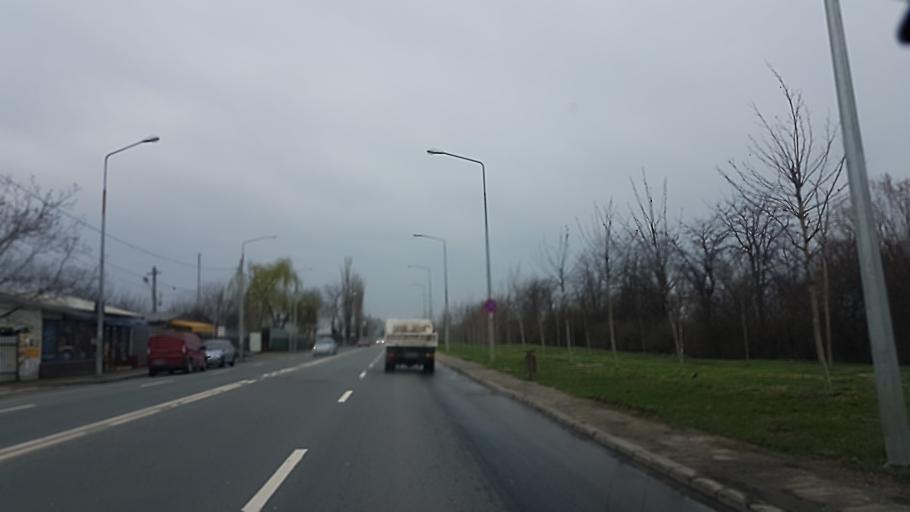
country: RO
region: Ilfov
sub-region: Comuna Pantelimon
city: Pantelimon
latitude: 44.4318
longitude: 26.2100
